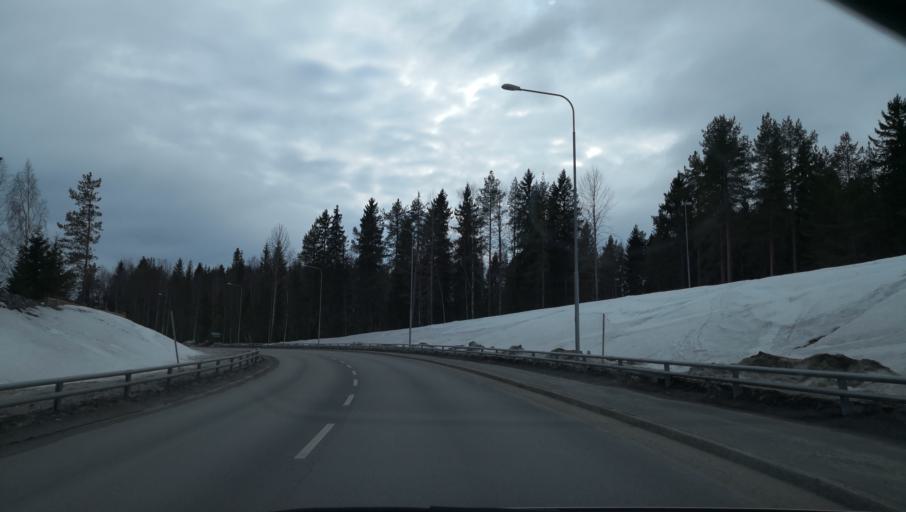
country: SE
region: Vaesterbotten
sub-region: Vannas Kommun
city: Vaennaes
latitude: 63.9128
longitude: 19.7701
